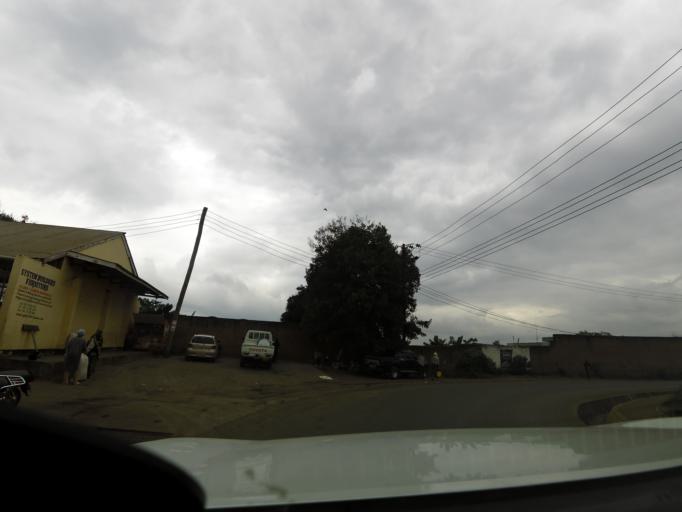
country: TZ
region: Arusha
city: Arusha
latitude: -3.3625
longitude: 36.6609
